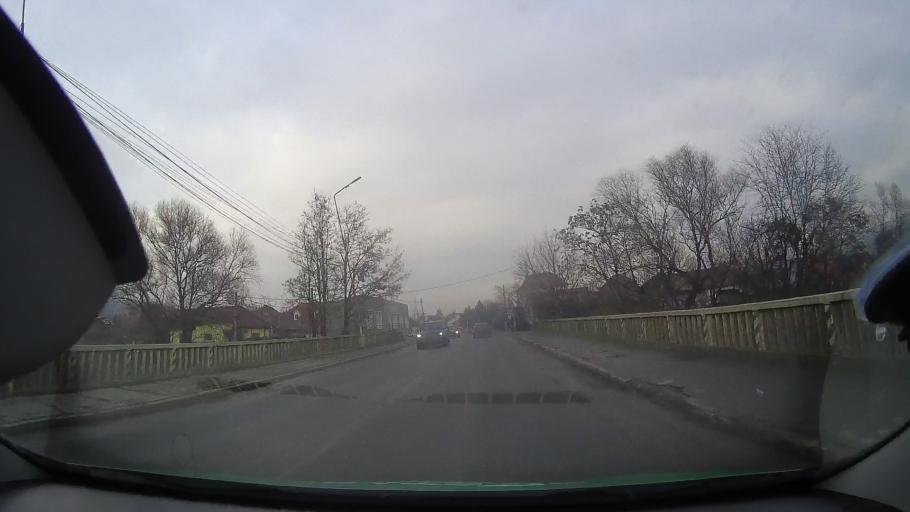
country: RO
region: Mures
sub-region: Comuna Ludus
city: Ludus
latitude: 46.4804
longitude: 24.0959
